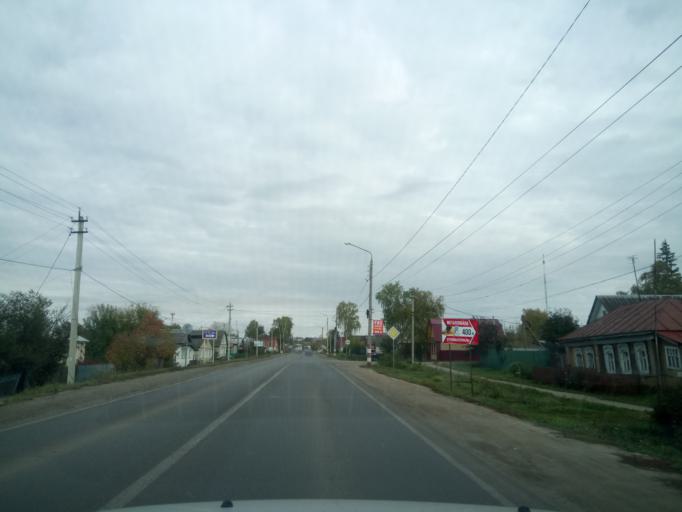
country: RU
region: Nizjnij Novgorod
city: Lukoyanov
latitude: 55.0311
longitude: 44.4839
